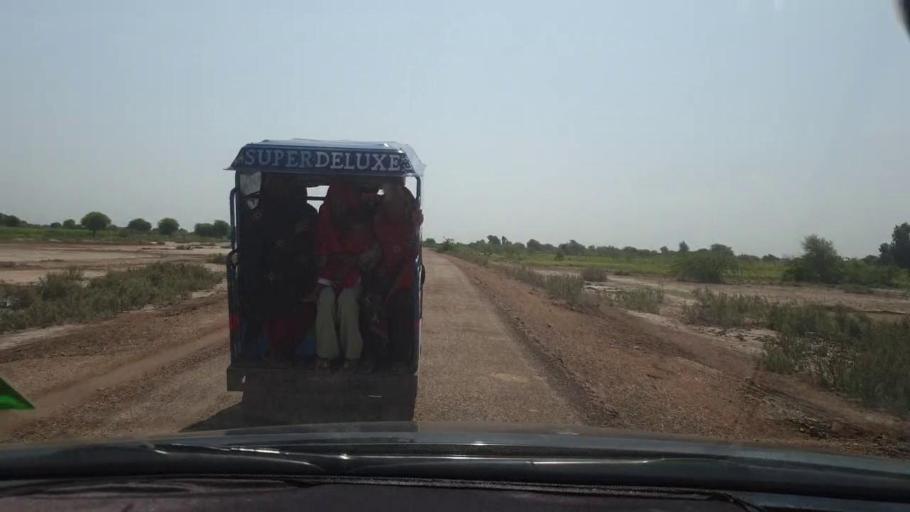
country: PK
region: Sindh
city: Tando Bago
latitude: 24.7934
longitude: 69.1682
